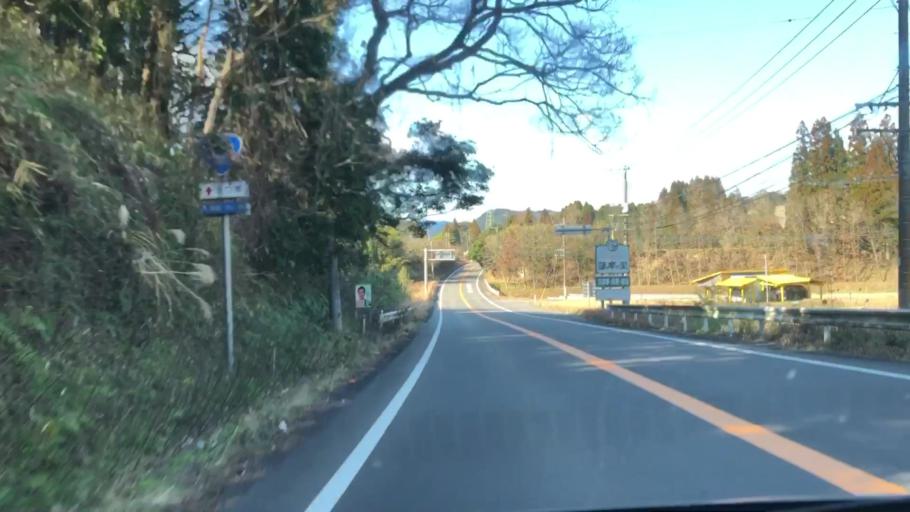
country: JP
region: Kagoshima
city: Satsumasendai
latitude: 31.8424
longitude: 130.4295
